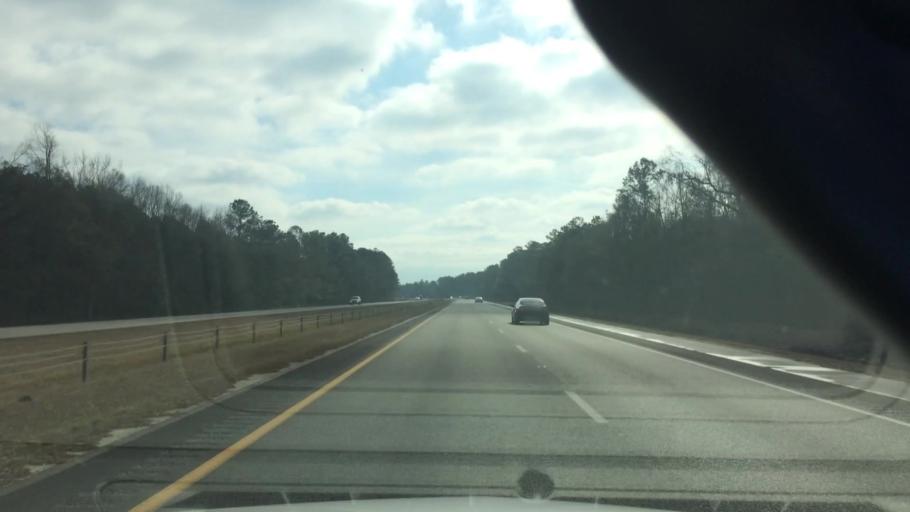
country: US
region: North Carolina
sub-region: Pender County
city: Burgaw
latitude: 34.5419
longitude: -77.8935
